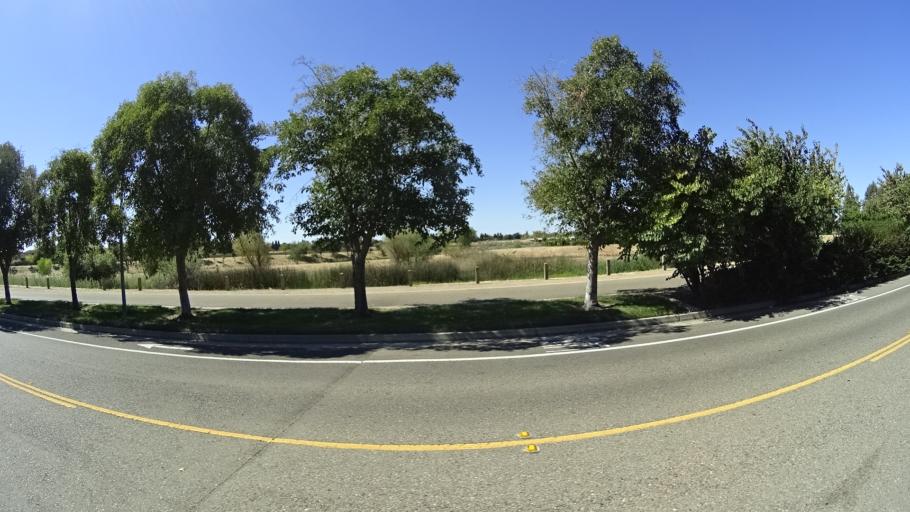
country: US
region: California
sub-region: Sacramento County
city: Laguna
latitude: 38.4327
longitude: -121.4060
